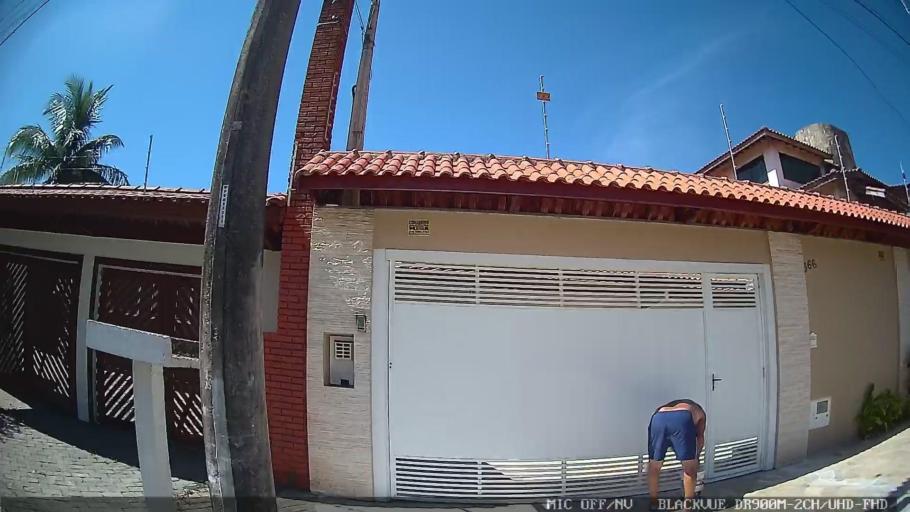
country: BR
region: Sao Paulo
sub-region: Peruibe
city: Peruibe
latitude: -24.3022
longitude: -46.9726
